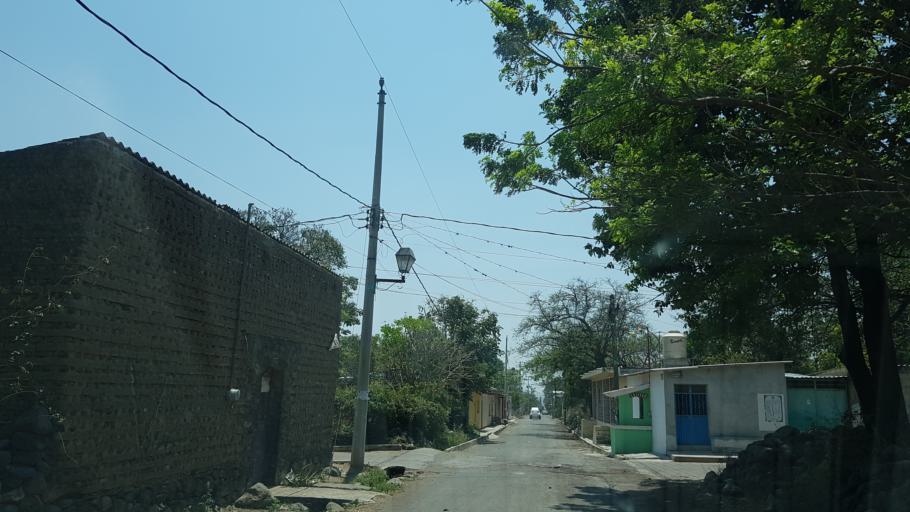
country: MX
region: Puebla
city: Huaquechula
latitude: 18.7760
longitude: -98.5452
